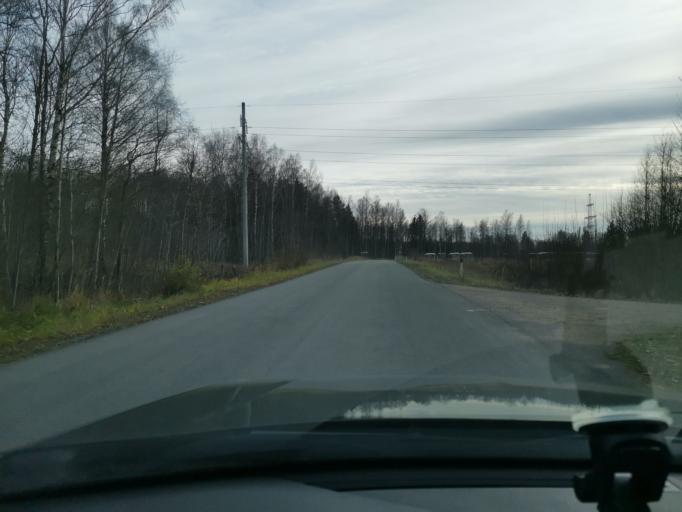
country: EE
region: Ida-Virumaa
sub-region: Sillamaee linn
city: Sillamae
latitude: 59.2720
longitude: 27.9127
